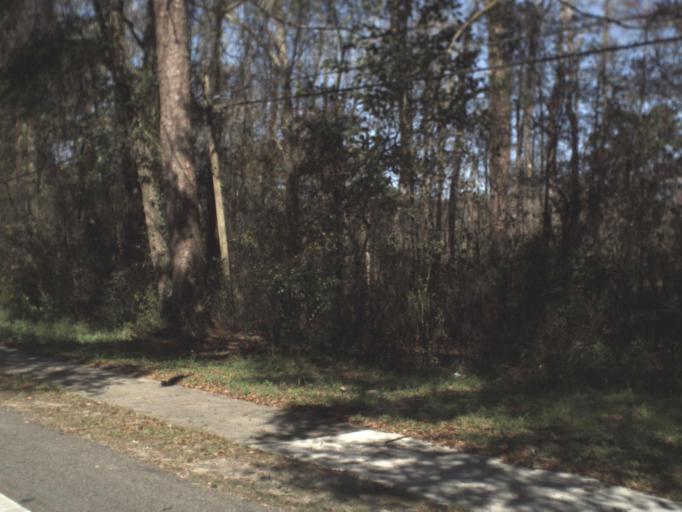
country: US
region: Florida
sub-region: Leon County
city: Tallahassee
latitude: 30.4126
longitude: -84.3147
